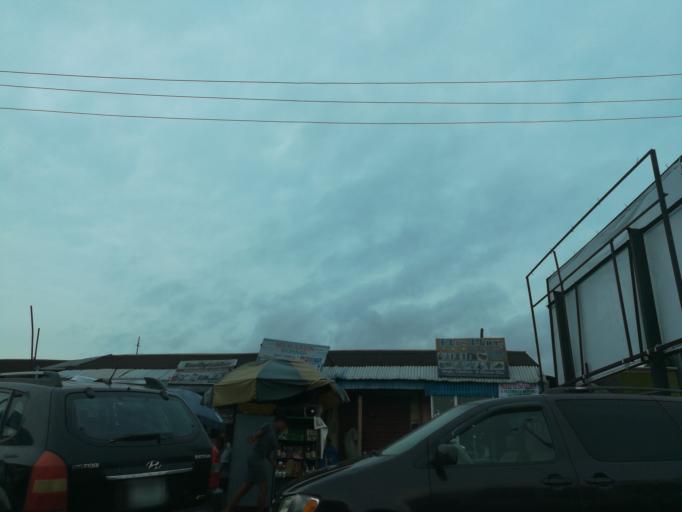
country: NG
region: Rivers
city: Port Harcourt
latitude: 4.8262
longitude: 7.0250
